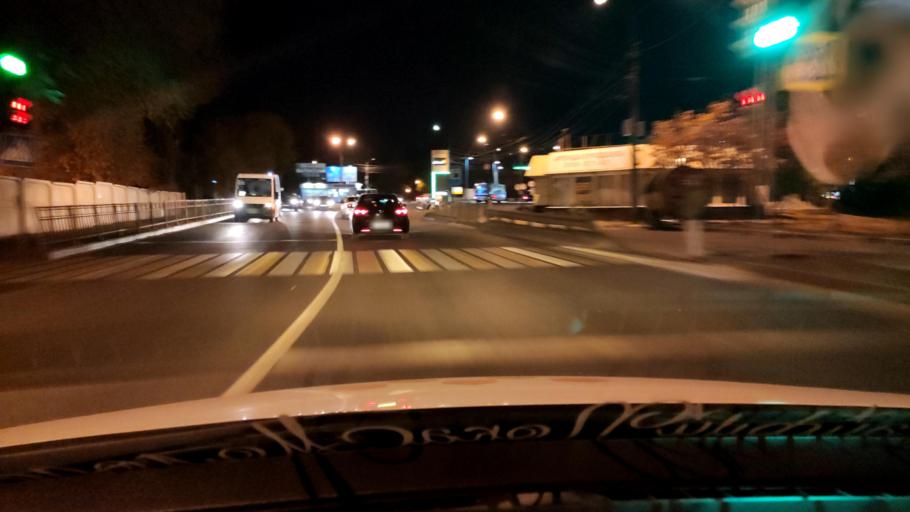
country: RU
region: Voronezj
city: Voronezh
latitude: 51.6923
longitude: 39.2061
